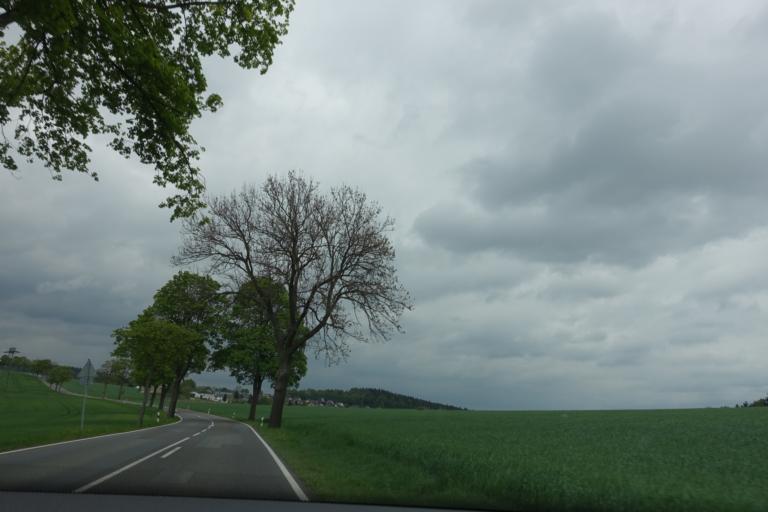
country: DE
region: Saxony
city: Bornichen
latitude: 50.7397
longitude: 13.1376
